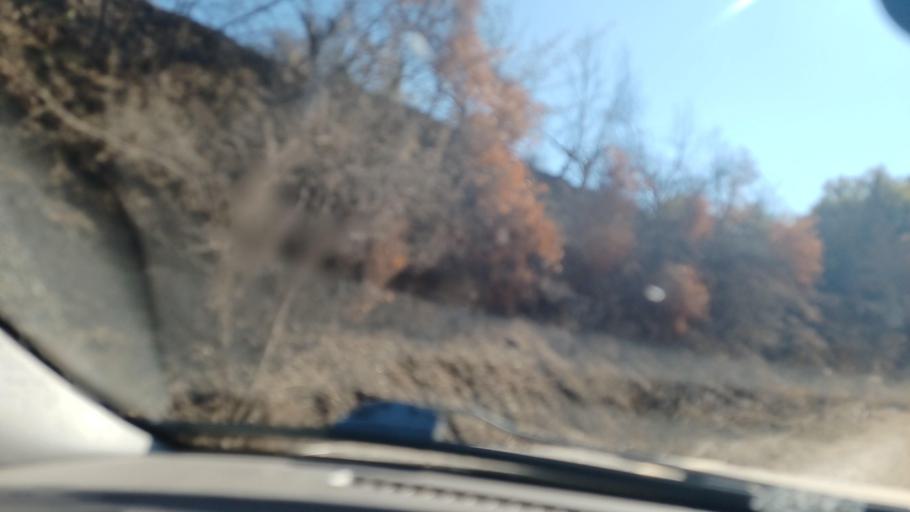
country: CY
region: Pafos
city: Polis
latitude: 34.9465
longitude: 32.4844
